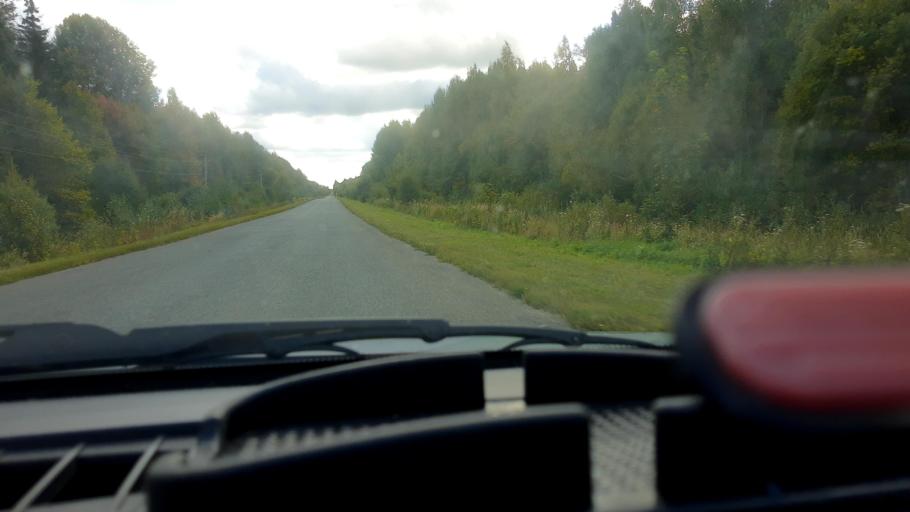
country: RU
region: Mariy-El
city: Kilemary
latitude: 56.9151
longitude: 46.7234
